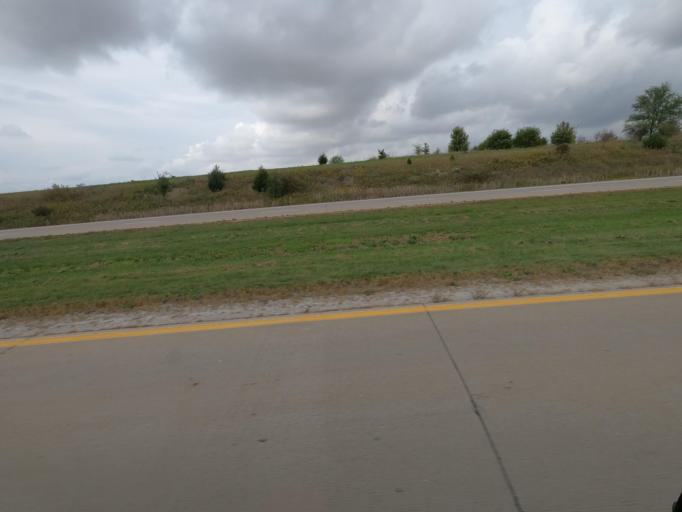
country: US
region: Iowa
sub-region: Wapello County
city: Ottumwa
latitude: 41.0039
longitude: -92.3059
